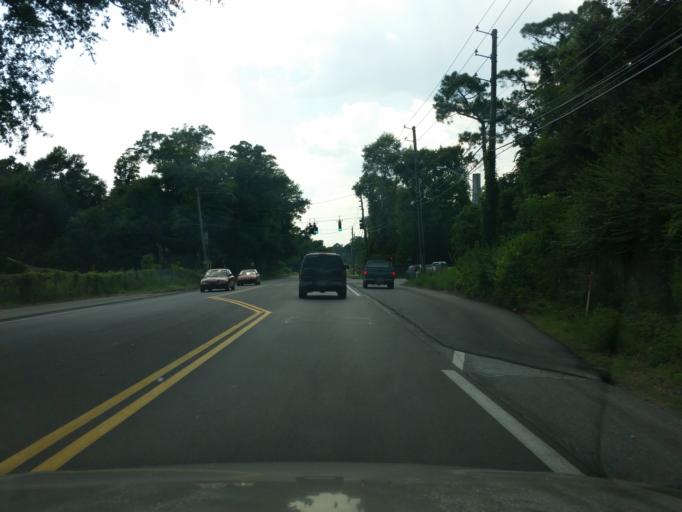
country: US
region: Florida
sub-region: Escambia County
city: Ferry Pass
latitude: 30.5109
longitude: -87.2371
